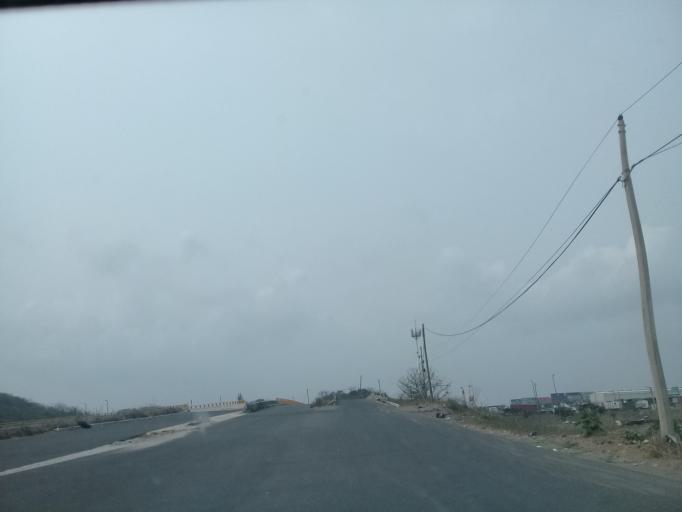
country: MX
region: Veracruz
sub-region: Veracruz
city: Colonia el Renacimiento
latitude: 19.2296
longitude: -96.2136
